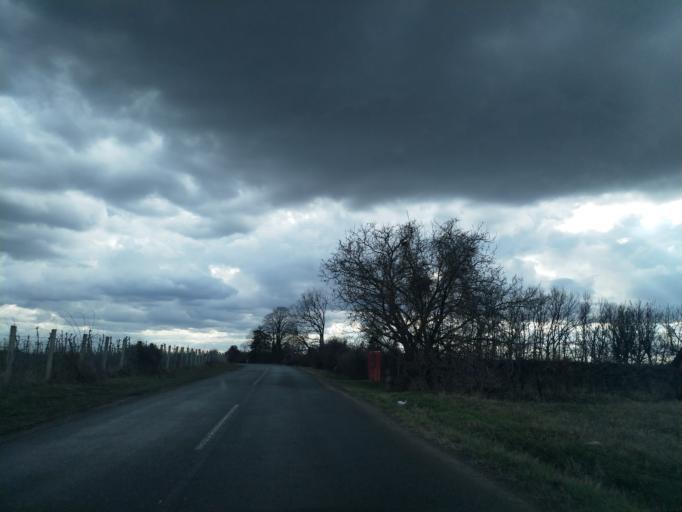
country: RS
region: Central Serbia
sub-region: Belgrade
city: Grocka
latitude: 44.6377
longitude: 20.7506
